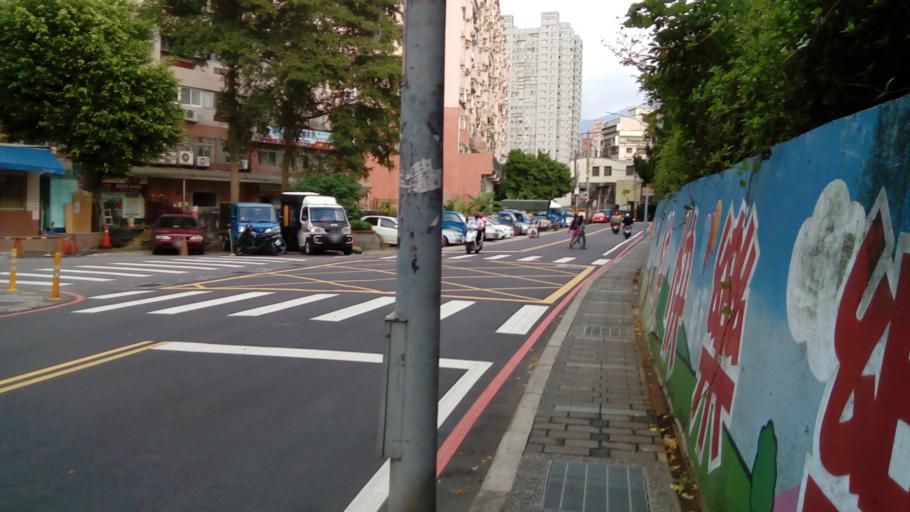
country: TW
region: Taipei
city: Taipei
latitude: 25.1796
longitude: 121.4405
